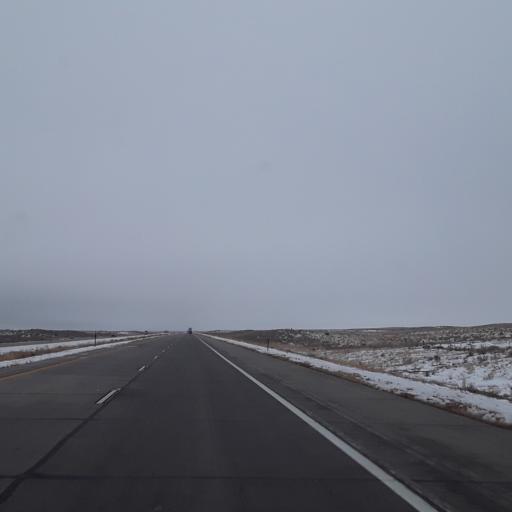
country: US
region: Colorado
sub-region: Logan County
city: Sterling
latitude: 40.5505
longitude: -103.2176
